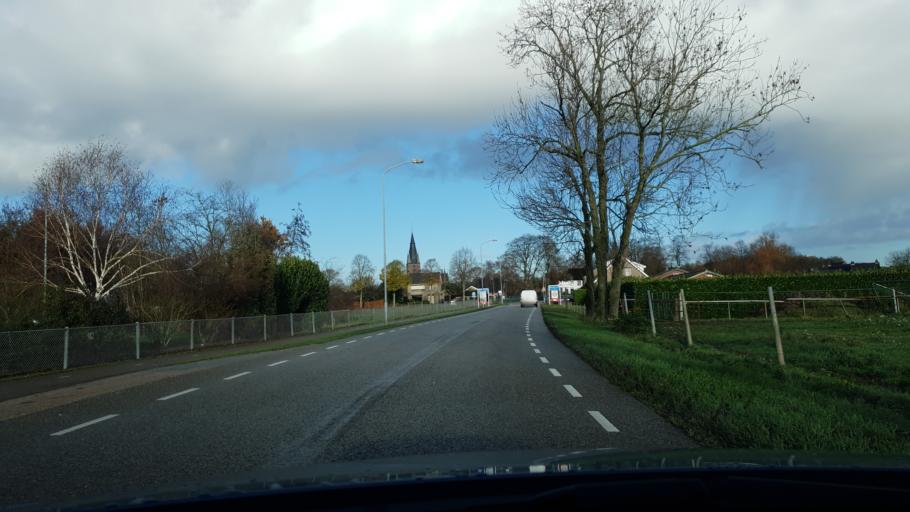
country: NL
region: Gelderland
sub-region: Gemeente Wijchen
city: Bergharen
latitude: 51.8467
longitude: 5.6682
